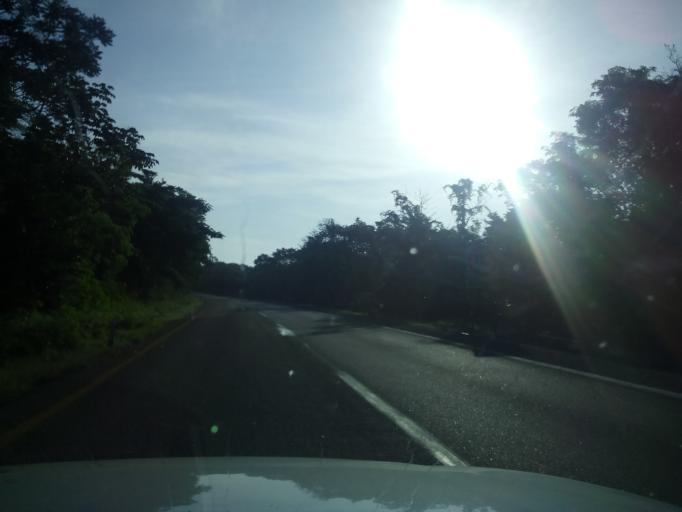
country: MX
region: Yucatan
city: Tinum
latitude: 20.7080
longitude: -88.4582
